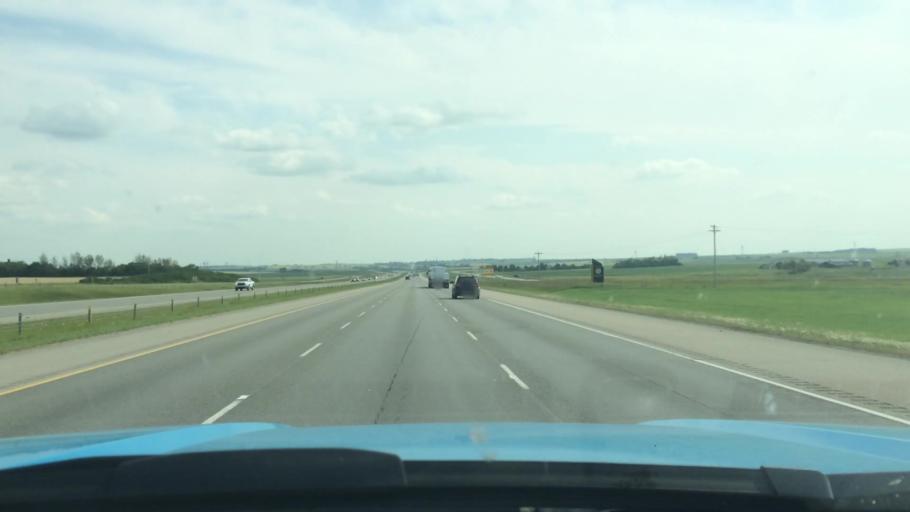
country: CA
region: Alberta
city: Crossfield
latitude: 51.4907
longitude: -114.0253
